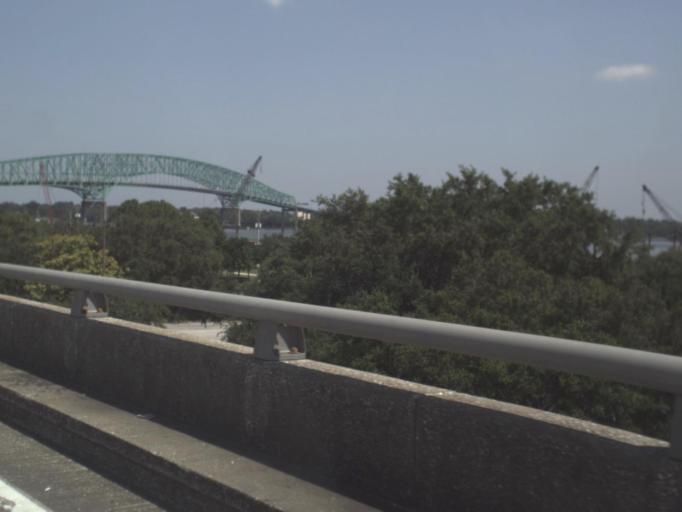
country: US
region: Florida
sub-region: Duval County
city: Jacksonville
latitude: 30.3208
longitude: -81.6369
